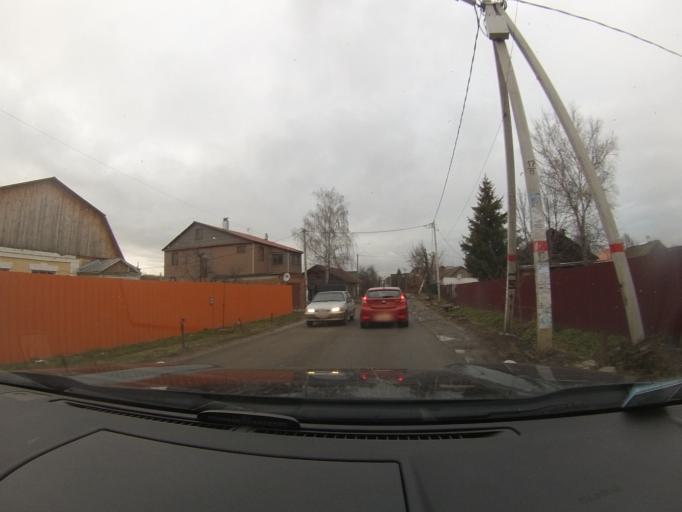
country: RU
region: Moskovskaya
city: Voskresensk
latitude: 55.3261
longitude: 38.6809
